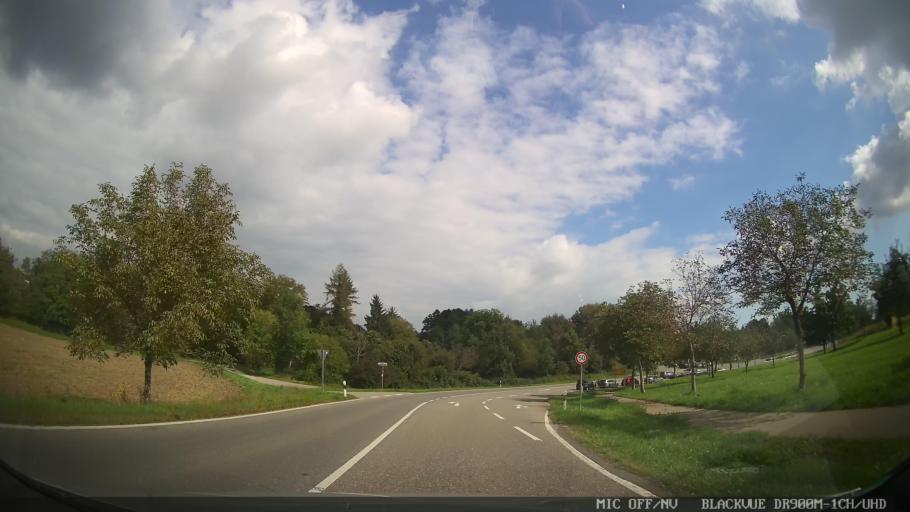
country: CH
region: Thurgau
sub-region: Kreuzlingen District
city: Gottlieben
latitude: 47.6983
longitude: 9.1344
